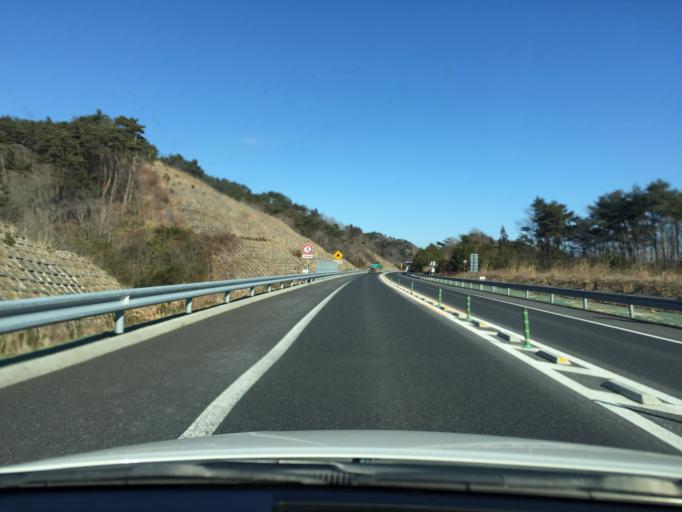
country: JP
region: Fukushima
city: Namie
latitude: 37.6828
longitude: 140.9174
